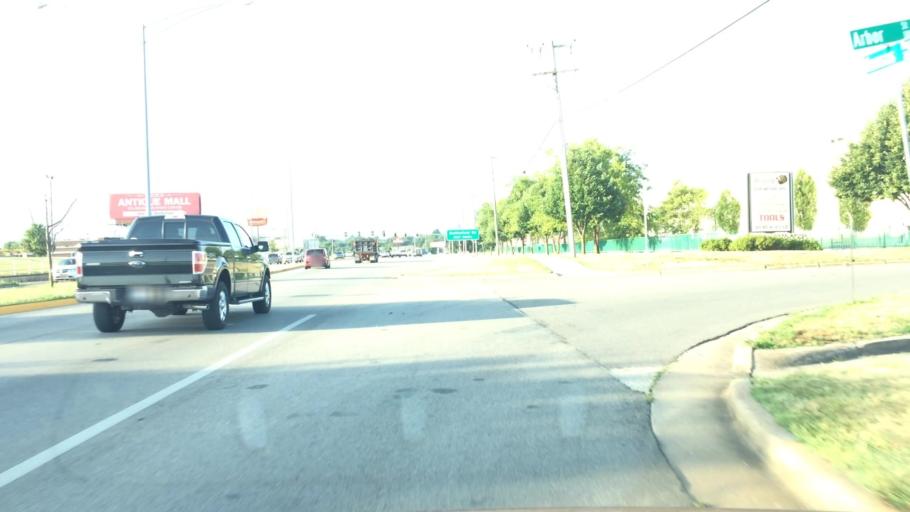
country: US
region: Missouri
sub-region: Greene County
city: Springfield
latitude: 37.1624
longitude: -93.3164
